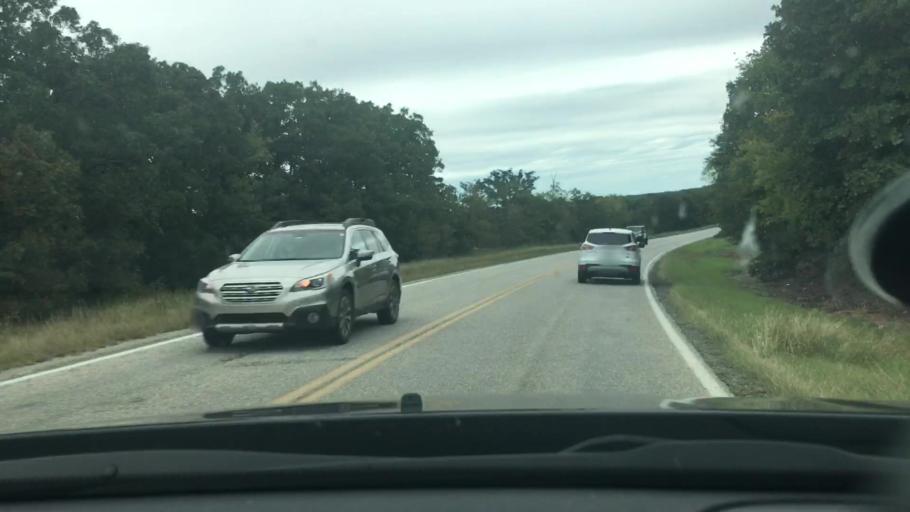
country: US
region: Oklahoma
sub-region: Johnston County
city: Tishomingo
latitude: 34.3222
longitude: -96.4243
